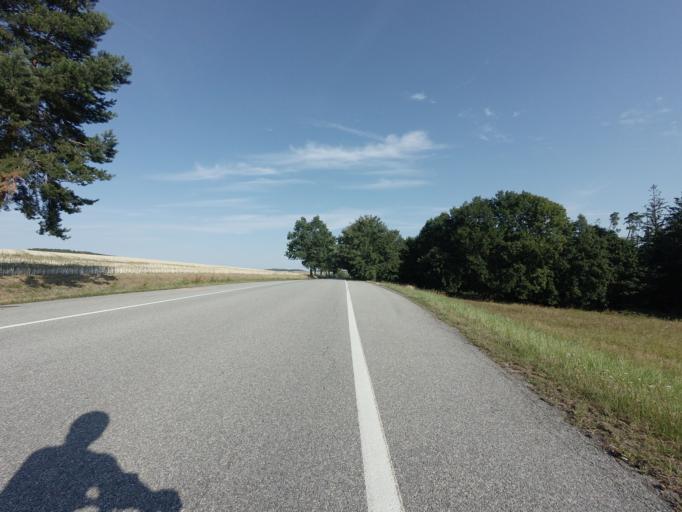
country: CZ
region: Jihocesky
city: Tyn nad Vltavou
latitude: 49.2699
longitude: 14.4076
